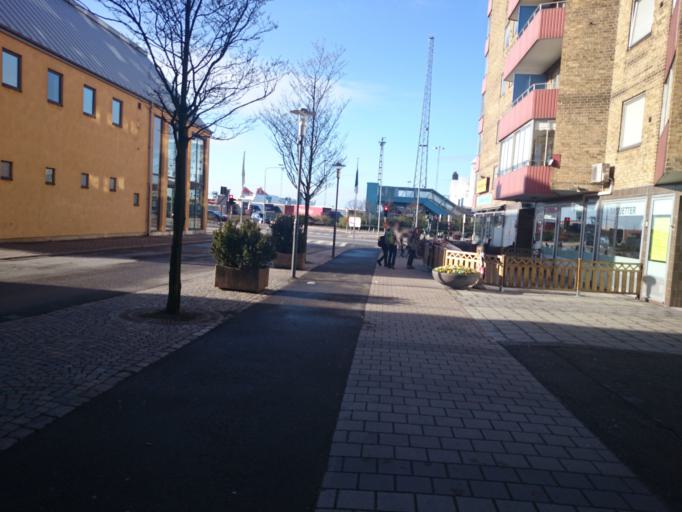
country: SE
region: Skane
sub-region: Trelleborgs Kommun
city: Trelleborg
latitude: 55.3735
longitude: 13.1559
